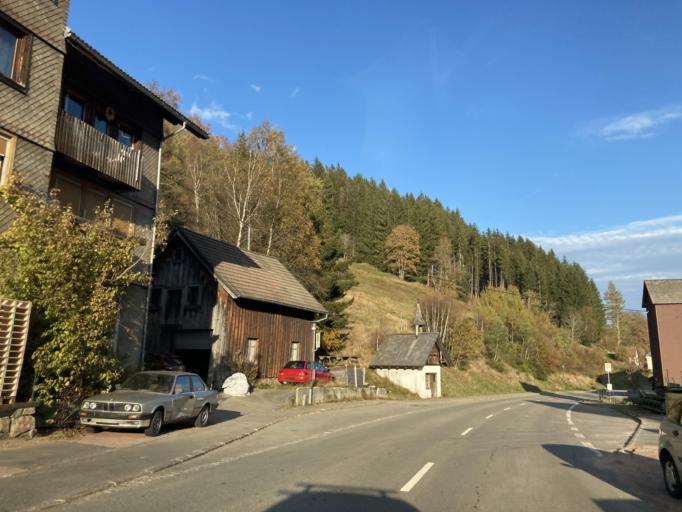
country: DE
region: Baden-Wuerttemberg
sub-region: Freiburg Region
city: Eisenbach
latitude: 48.0063
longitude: 8.2616
